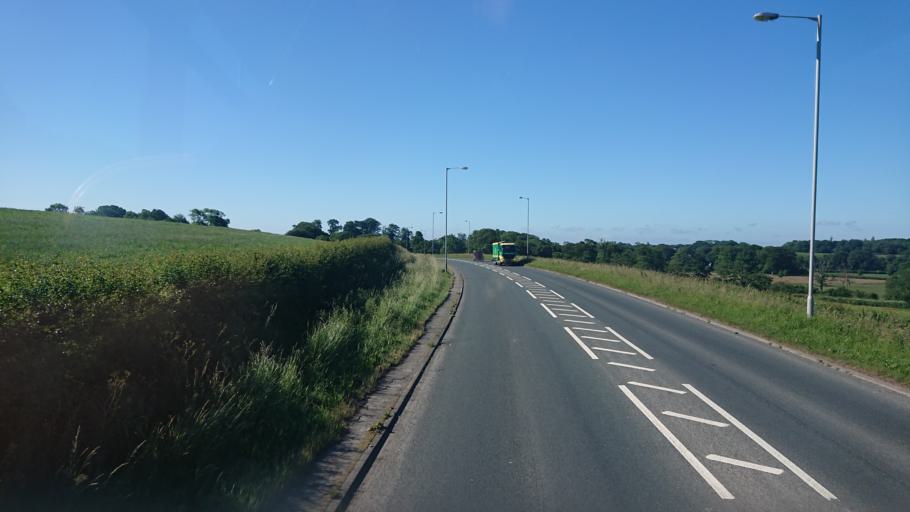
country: GB
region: England
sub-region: Lancashire
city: Galgate
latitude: 53.9764
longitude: -2.7850
